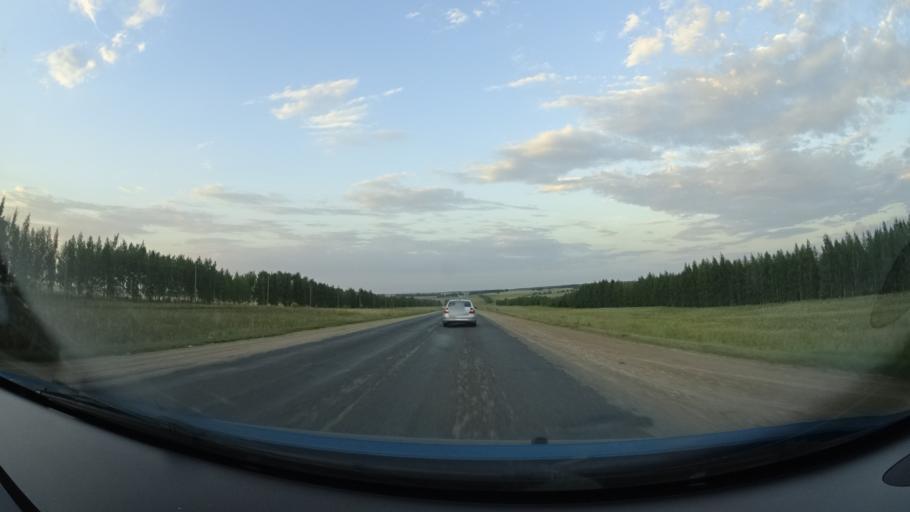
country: RU
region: Orenburg
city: Severnoye
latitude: 54.2279
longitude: 52.7580
